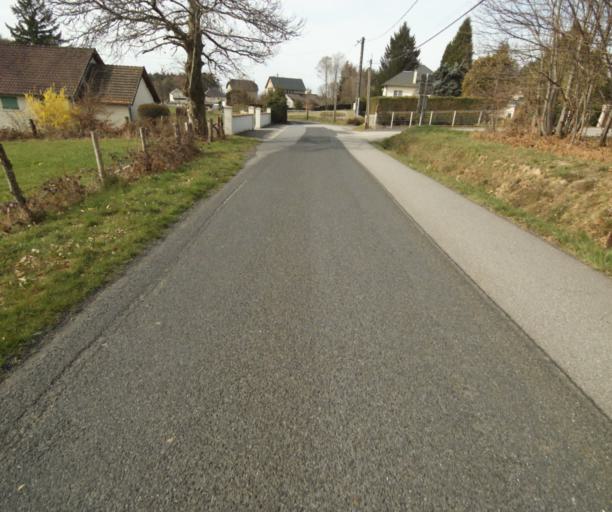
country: FR
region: Limousin
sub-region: Departement de la Correze
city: Correze
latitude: 45.4213
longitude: 1.8316
